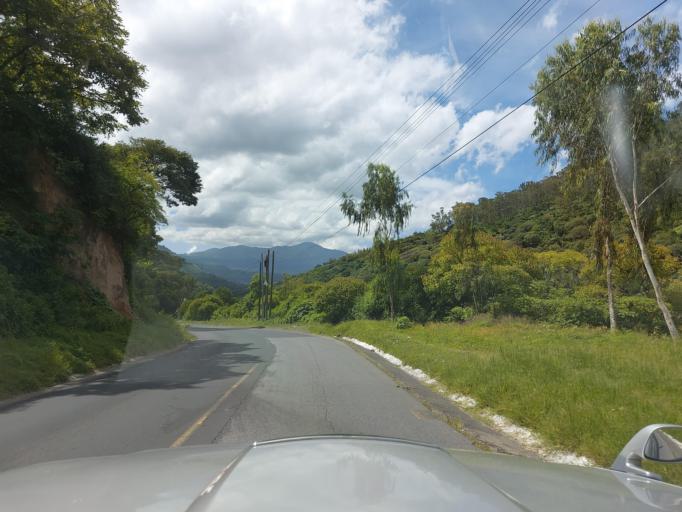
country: GT
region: Sacatepequez
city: Pastores
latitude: 14.6079
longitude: -90.7684
